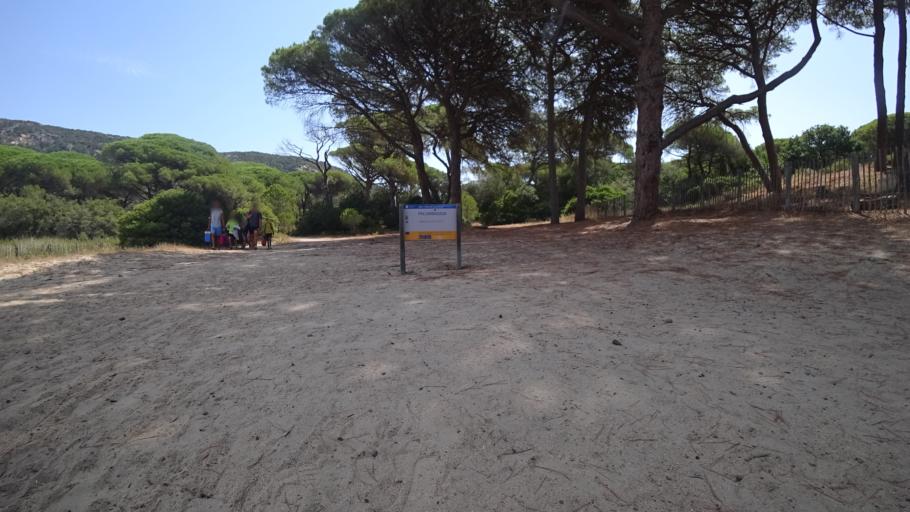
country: FR
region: Corsica
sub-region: Departement de la Corse-du-Sud
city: Porto-Vecchio
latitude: 41.5600
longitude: 9.3363
